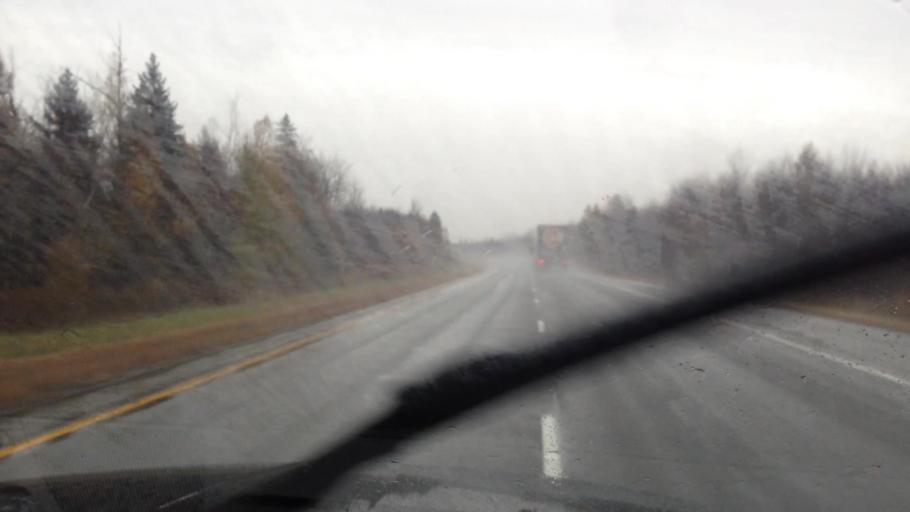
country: CA
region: Ontario
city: Casselman
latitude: 45.3121
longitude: -75.2149
